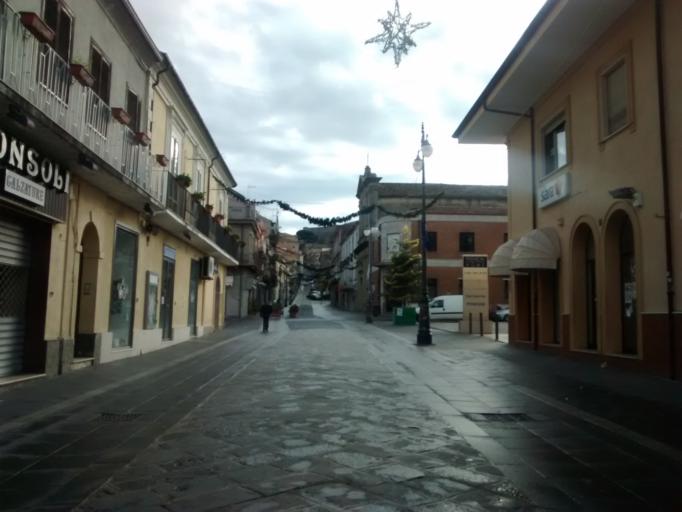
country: IT
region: Calabria
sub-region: Provincia di Vibo-Valentia
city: Vibo Valentia
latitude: 38.6736
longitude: 16.1017
